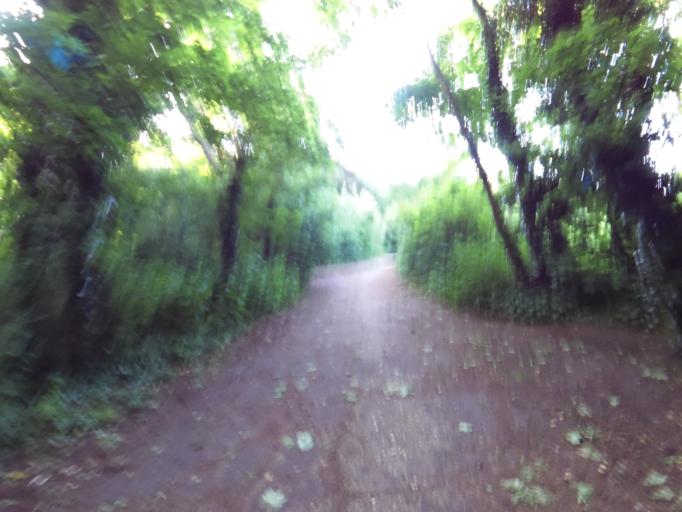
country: GB
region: England
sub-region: Suffolk
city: Kesgrave
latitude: 52.0648
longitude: 1.2652
